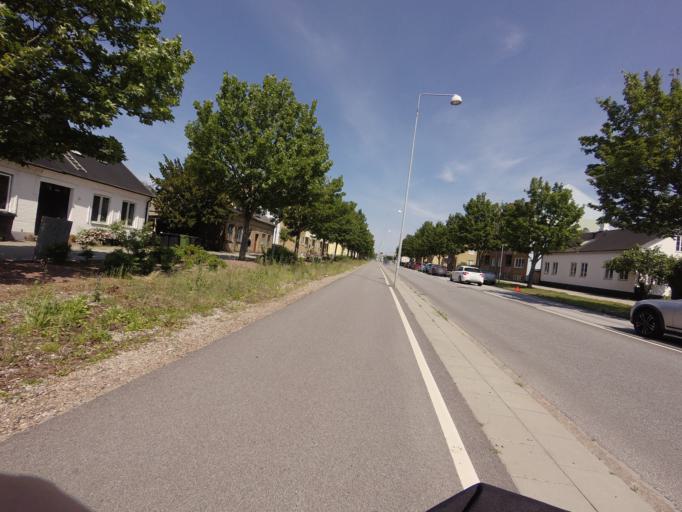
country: SE
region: Skane
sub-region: Malmo
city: Bunkeflostrand
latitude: 55.5802
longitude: 12.9291
